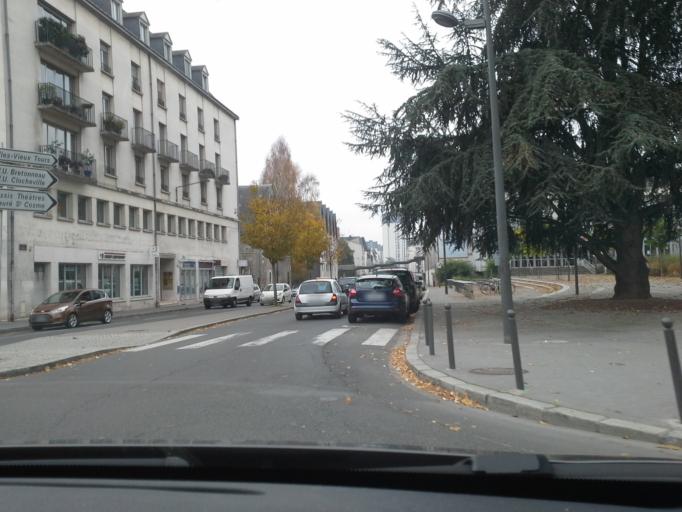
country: FR
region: Centre
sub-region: Departement d'Indre-et-Loire
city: Tours
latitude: 47.3964
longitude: 0.6838
